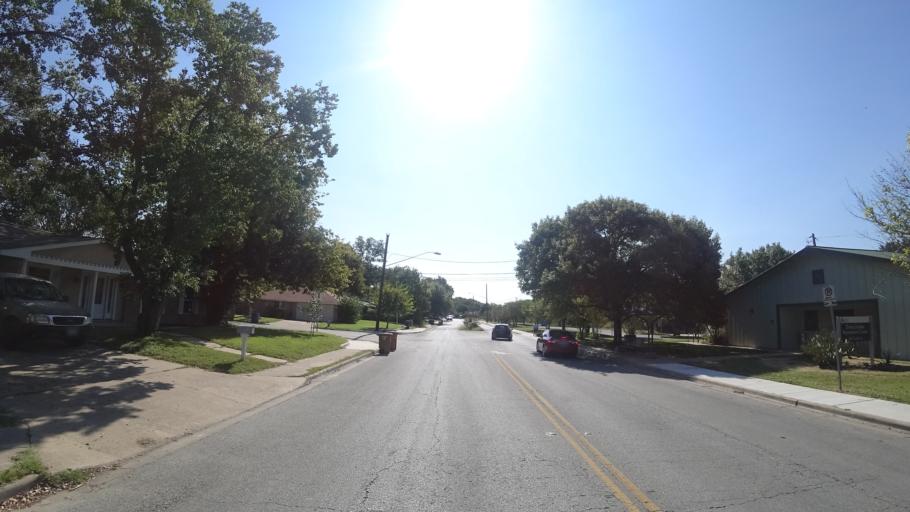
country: US
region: Texas
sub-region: Travis County
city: Austin
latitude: 30.3144
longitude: -97.6734
